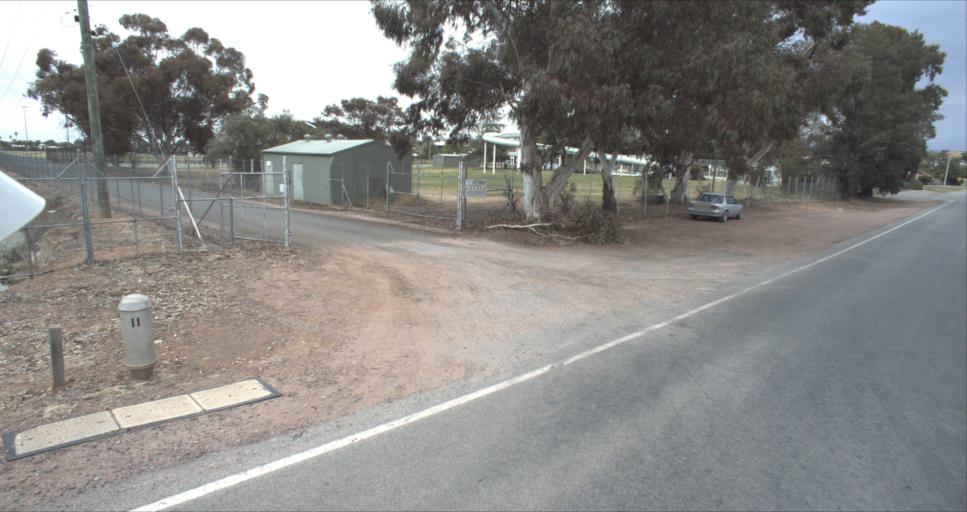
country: AU
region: New South Wales
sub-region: Leeton
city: Leeton
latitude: -34.5499
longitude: 146.4138
